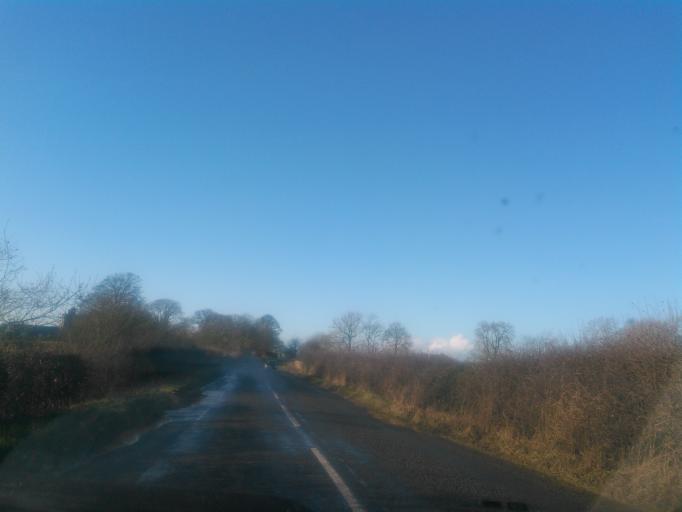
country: GB
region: England
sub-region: Shropshire
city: Prees
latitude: 52.8680
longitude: -2.6747
